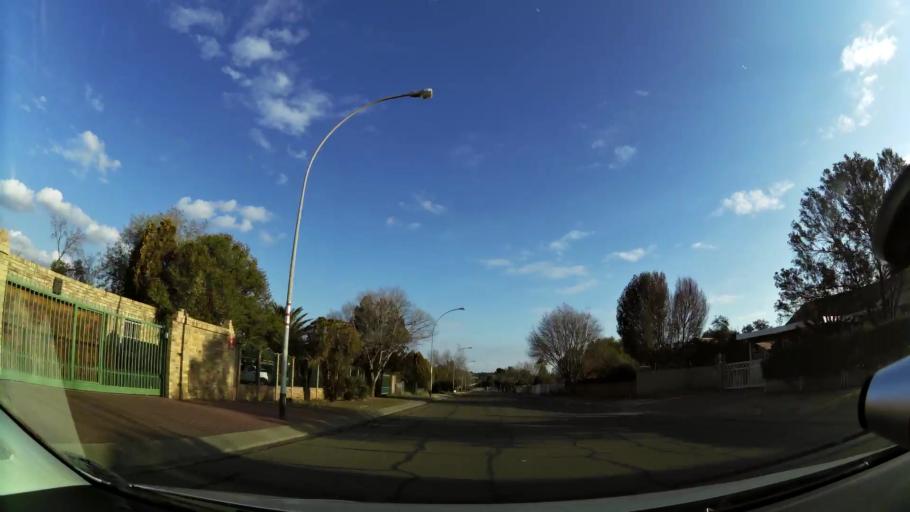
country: ZA
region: Orange Free State
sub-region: Mangaung Metropolitan Municipality
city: Bloemfontein
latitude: -29.1571
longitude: 26.1827
